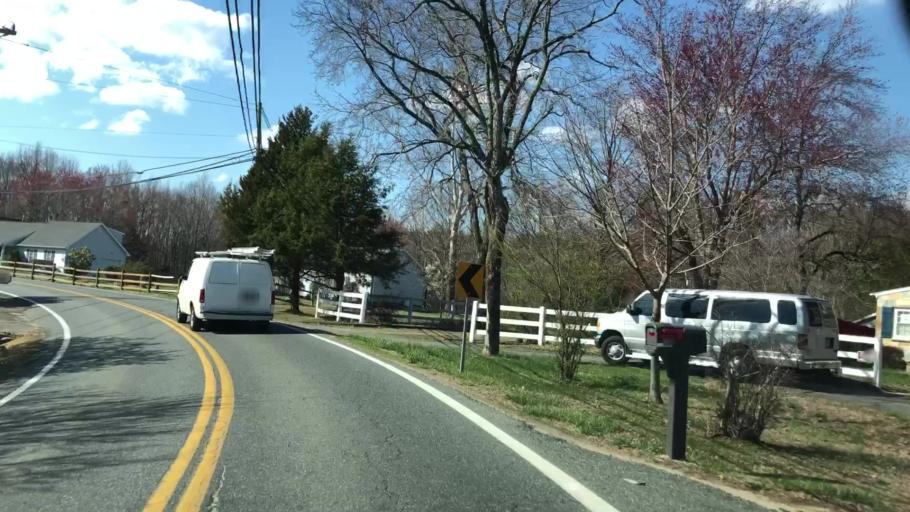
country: US
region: Virginia
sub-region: Stafford County
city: Falmouth
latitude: 38.3500
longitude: -77.4740
